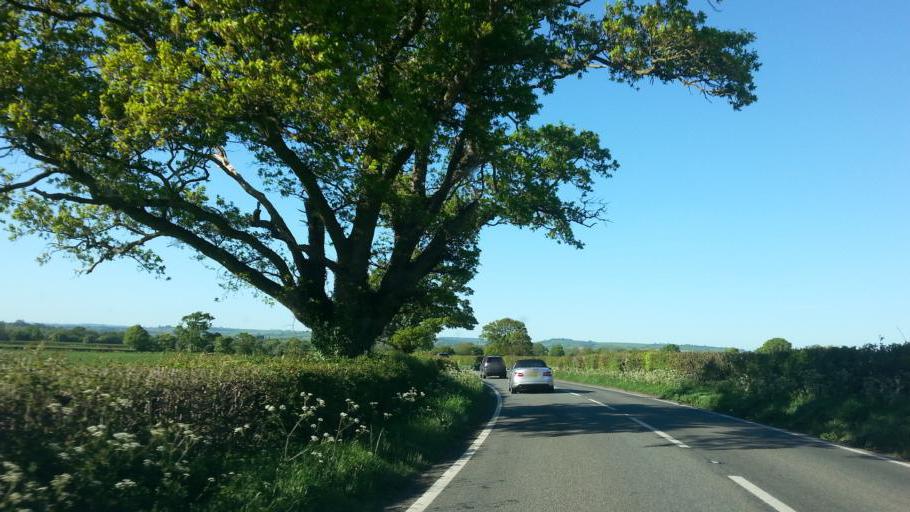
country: GB
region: England
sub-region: Somerset
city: Castle Cary
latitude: 51.1088
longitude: -2.5207
